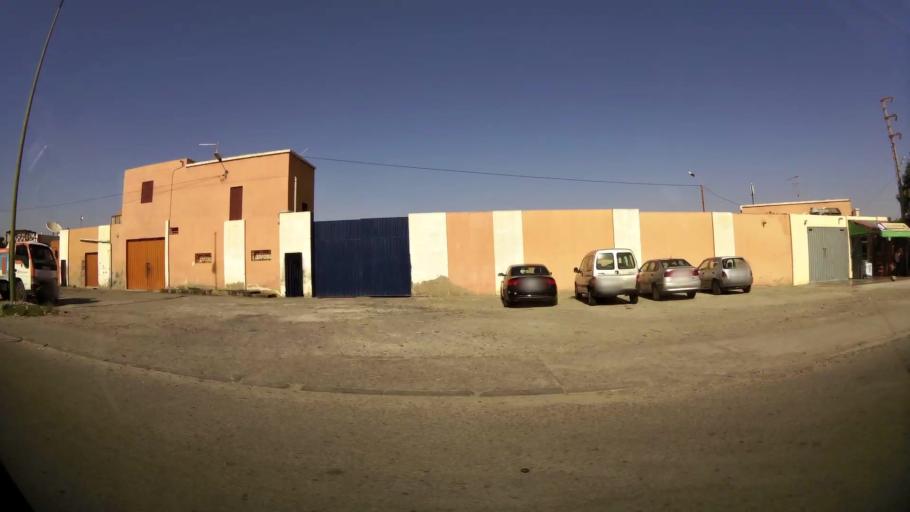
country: MA
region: Souss-Massa-Draa
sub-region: Inezgane-Ait Mellou
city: Inezgane
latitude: 30.3812
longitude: -9.5185
